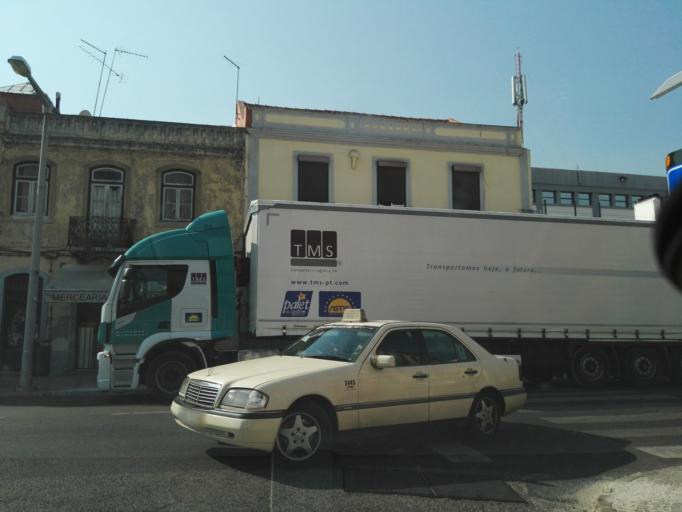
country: PT
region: Lisbon
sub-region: Lisbon
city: Lisbon
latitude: 38.7351
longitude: -9.1170
